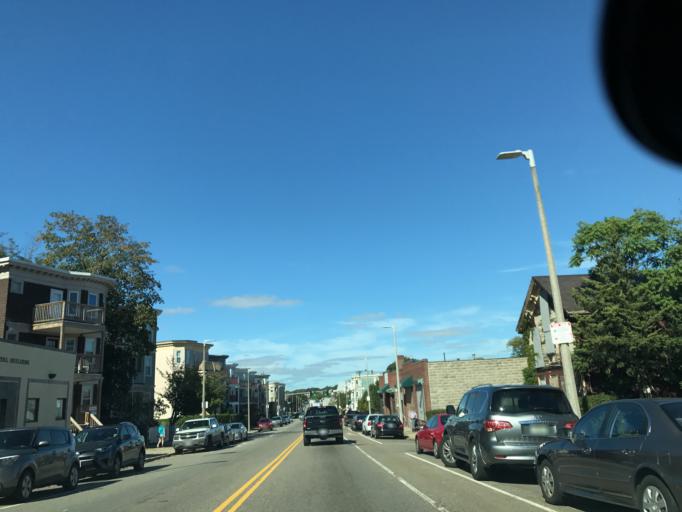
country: US
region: Massachusetts
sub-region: Suffolk County
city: South Boston
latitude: 42.2950
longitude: -71.0532
